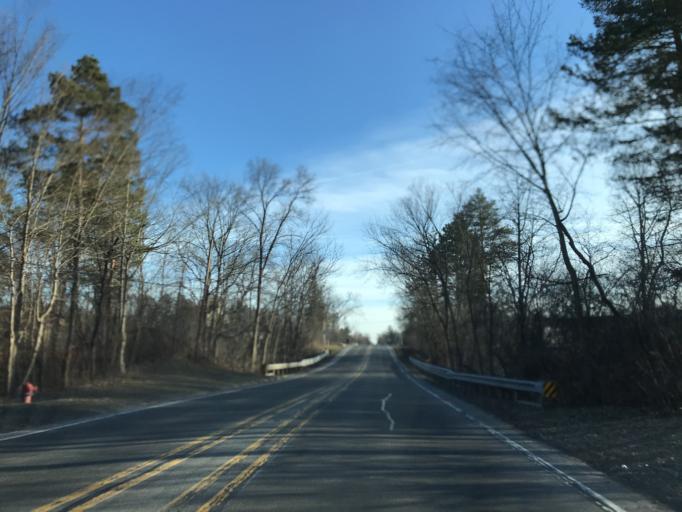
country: US
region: Michigan
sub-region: Oakland County
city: Franklin
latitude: 42.4702
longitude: -83.3182
